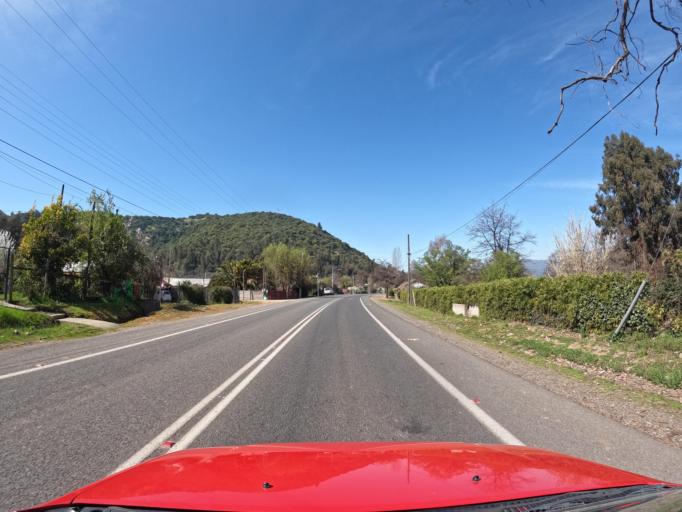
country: CL
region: Maule
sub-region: Provincia de Curico
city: Teno
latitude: -34.9781
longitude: -70.9869
